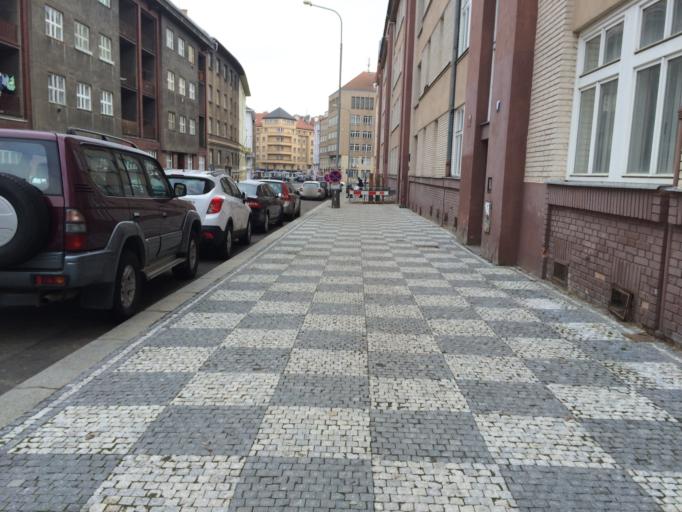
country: CZ
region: Praha
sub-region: Praha 1
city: Mala Strana
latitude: 50.0989
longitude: 14.3938
